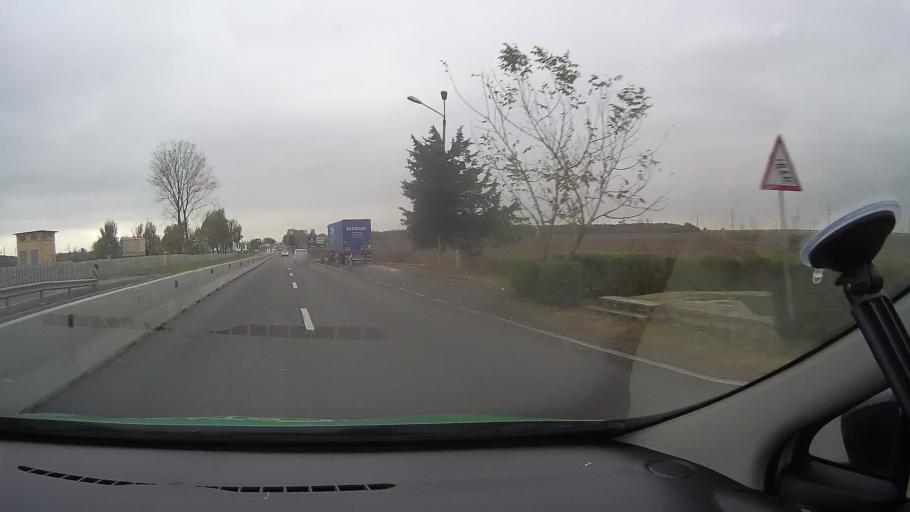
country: RO
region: Constanta
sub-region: Comuna Cumpana
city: Cumpana
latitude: 44.1684
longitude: 28.5724
